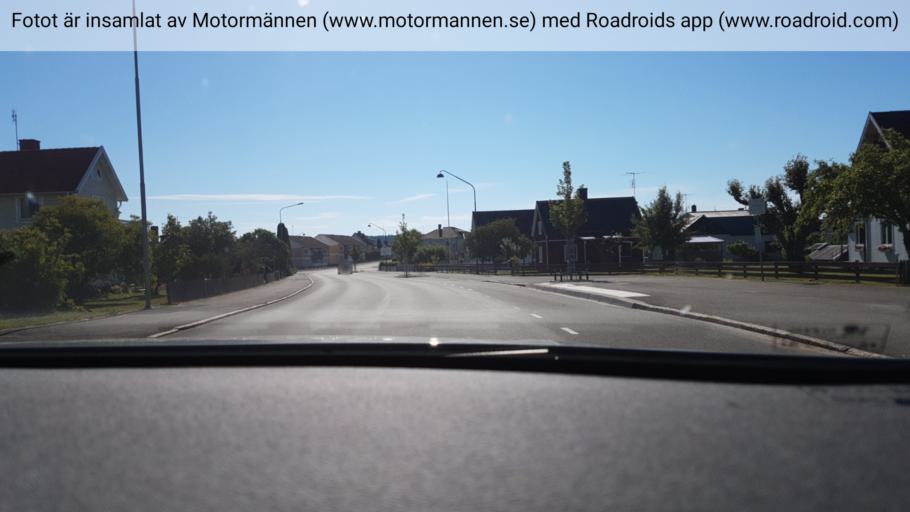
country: SE
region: Vaestra Goetaland
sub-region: Tidaholms Kommun
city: Tidaholm
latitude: 58.1873
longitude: 13.9536
